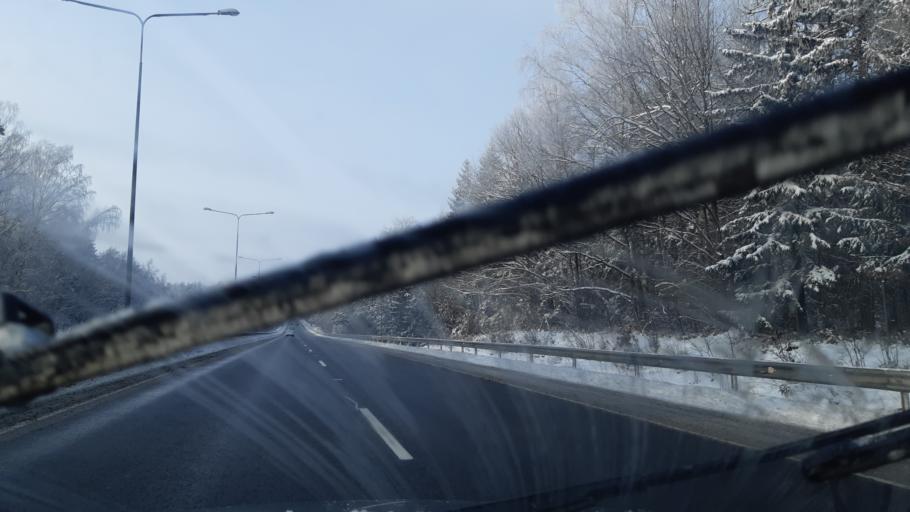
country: LT
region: Kauno apskritis
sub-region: Kauno rajonas
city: Karmelava
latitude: 54.9018
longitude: 24.1322
